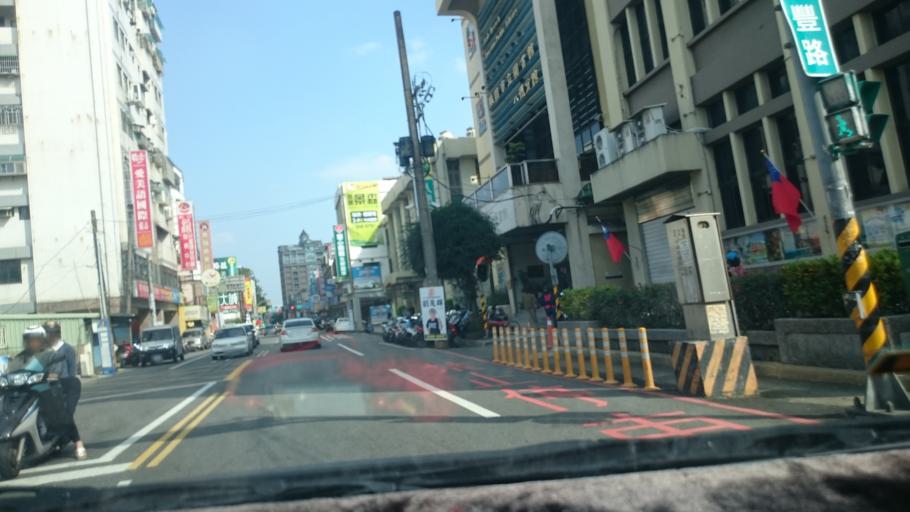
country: TW
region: Taiwan
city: Daxi
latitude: 24.9291
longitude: 121.2846
